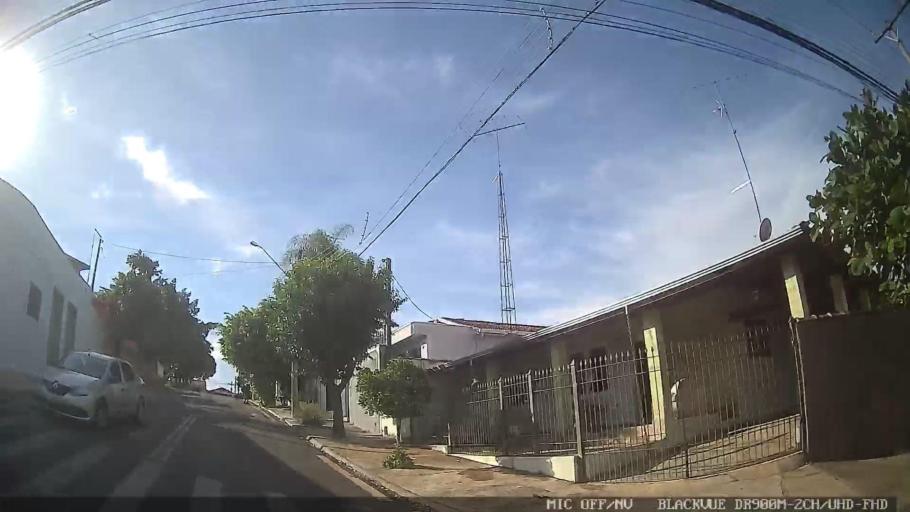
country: BR
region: Sao Paulo
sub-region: Tiete
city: Tiete
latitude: -23.0940
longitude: -47.7009
